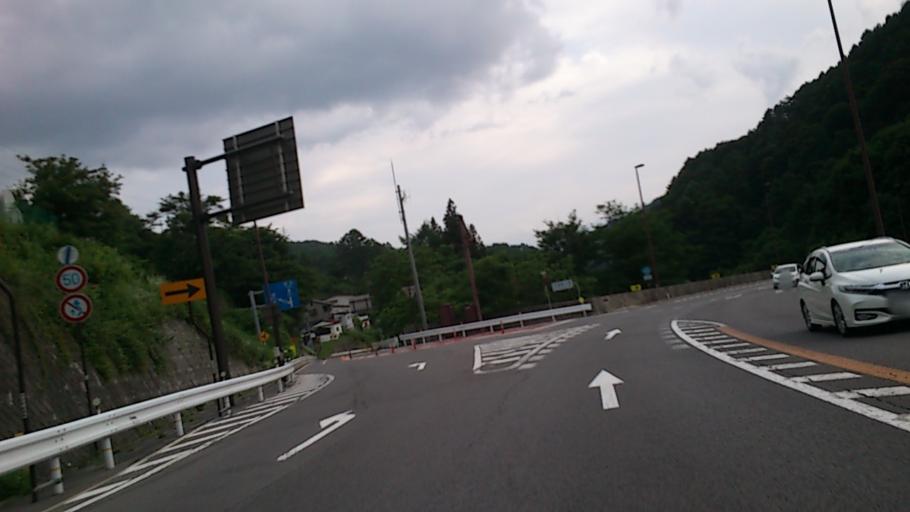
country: JP
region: Nagano
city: Okaya
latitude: 36.1035
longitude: 138.0941
